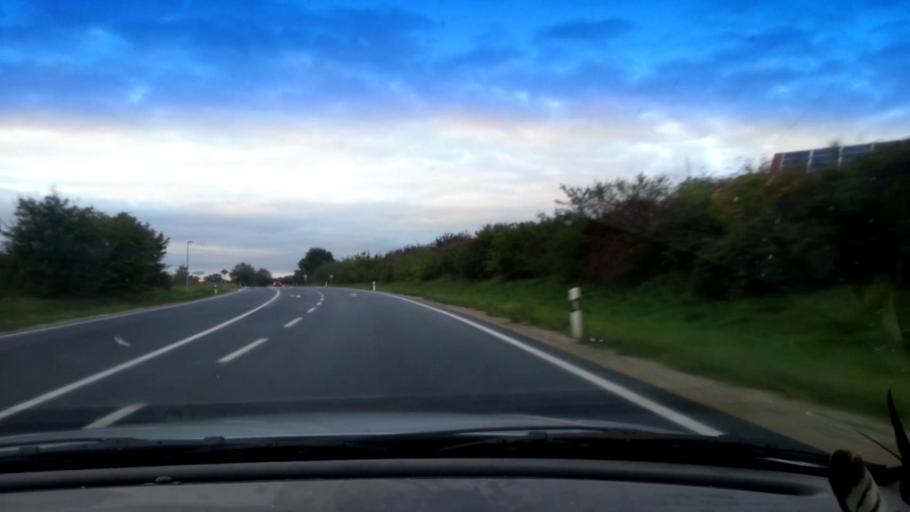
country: DE
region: Bavaria
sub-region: Upper Franconia
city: Stegaurach
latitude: 49.8608
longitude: 10.8599
